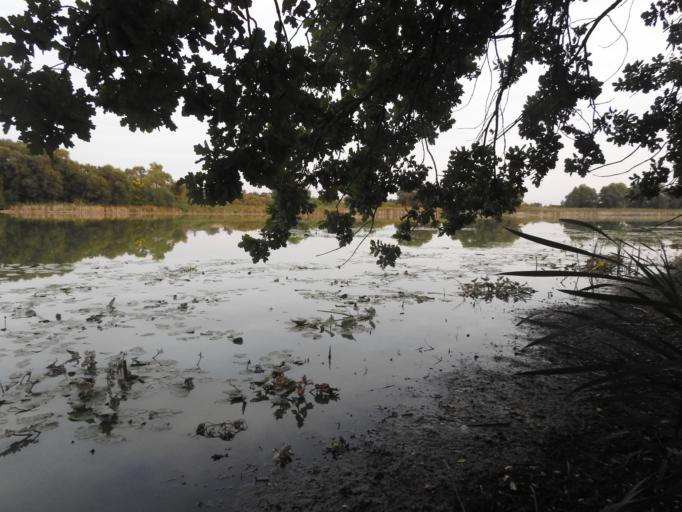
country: RU
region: Saratov
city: Lysyye Gory
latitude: 51.2548
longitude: 45.0060
